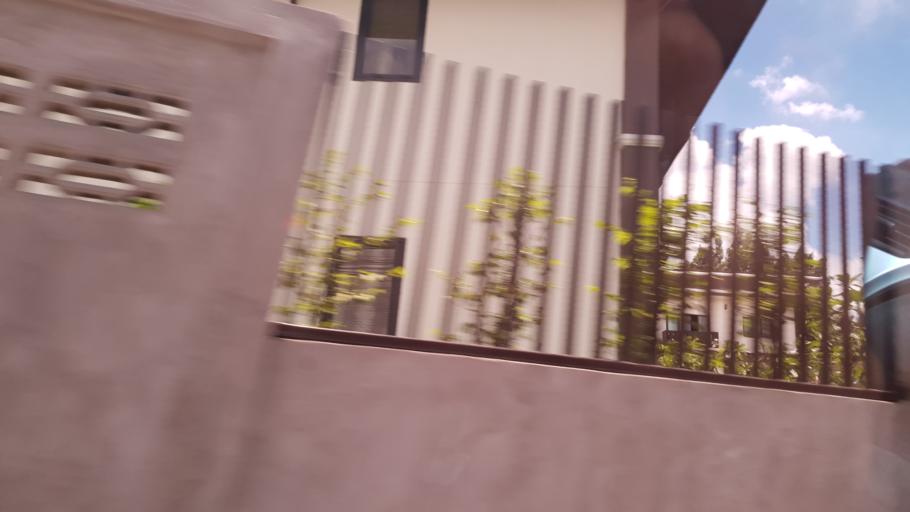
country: TH
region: Chiang Mai
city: Chiang Mai
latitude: 18.7751
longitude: 98.9875
